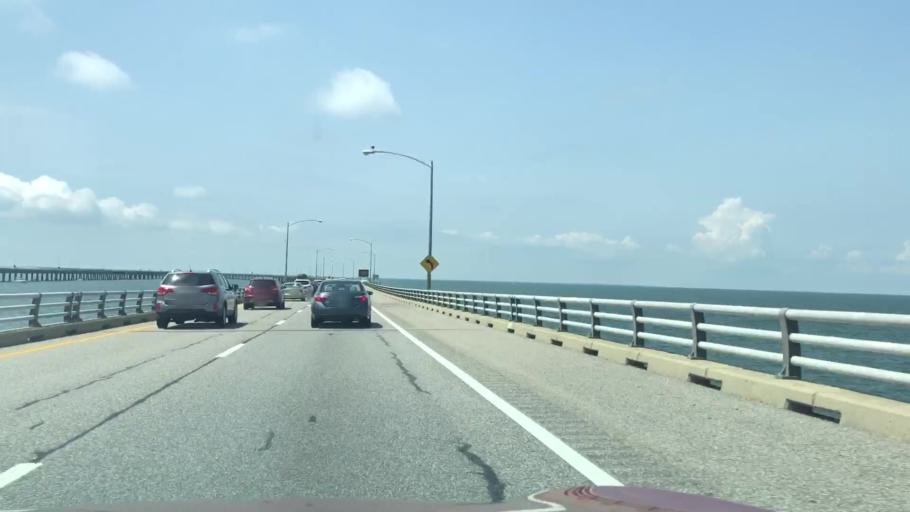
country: US
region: Virginia
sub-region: Northampton County
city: Cape Charles
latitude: 37.0885
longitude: -75.9958
